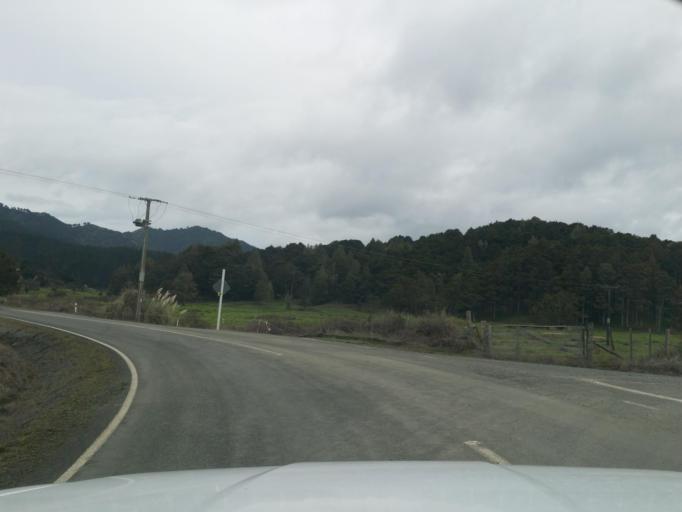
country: NZ
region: Northland
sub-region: Kaipara District
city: Dargaville
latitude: -35.8084
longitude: 173.9988
